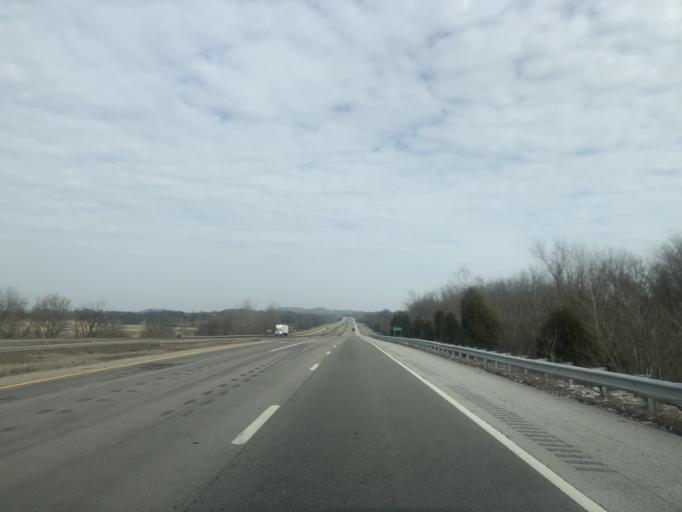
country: US
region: Tennessee
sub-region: Maury County
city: Mount Pleasant
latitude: 35.5801
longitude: -87.1434
